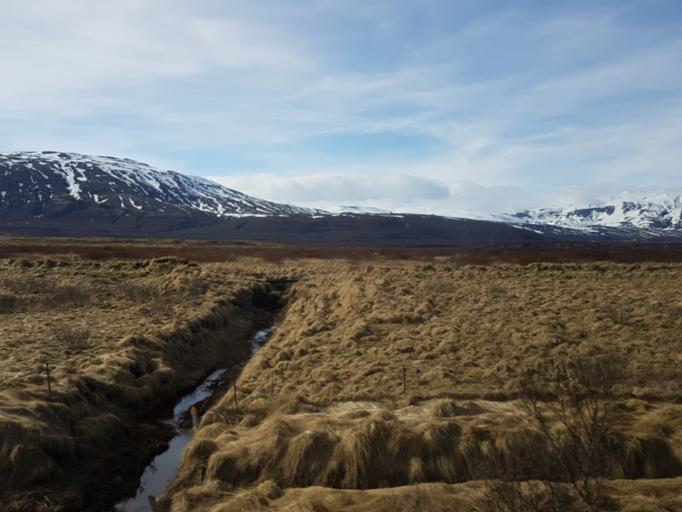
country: IS
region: South
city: Selfoss
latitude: 64.2441
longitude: -20.5014
